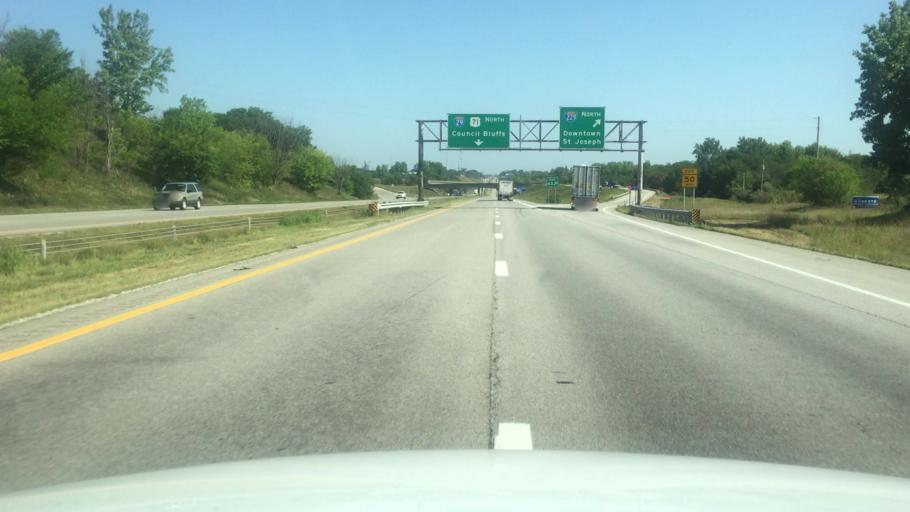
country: US
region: Missouri
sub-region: Buchanan County
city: Saint Joseph
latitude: 39.7028
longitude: -94.7882
